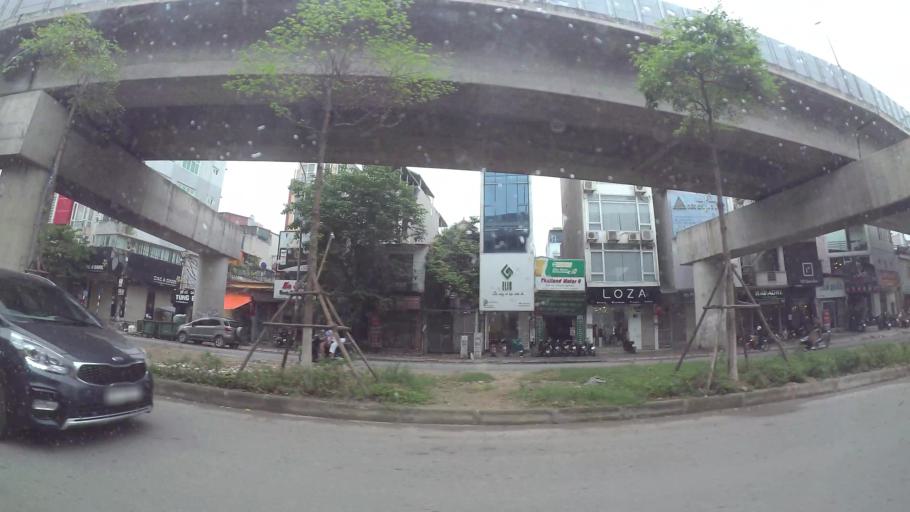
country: VN
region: Ha Noi
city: Dong Da
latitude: 21.0100
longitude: 105.8156
